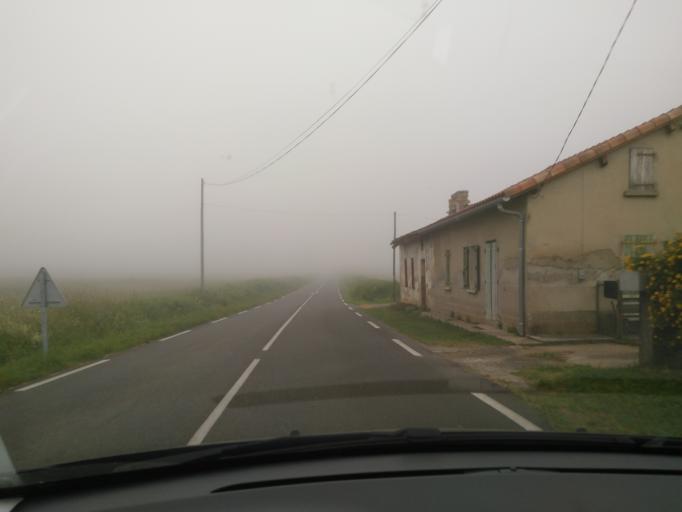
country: FR
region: Aquitaine
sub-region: Departement des Landes
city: Villeneuve-de-Marsan
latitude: 43.8865
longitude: -0.3318
